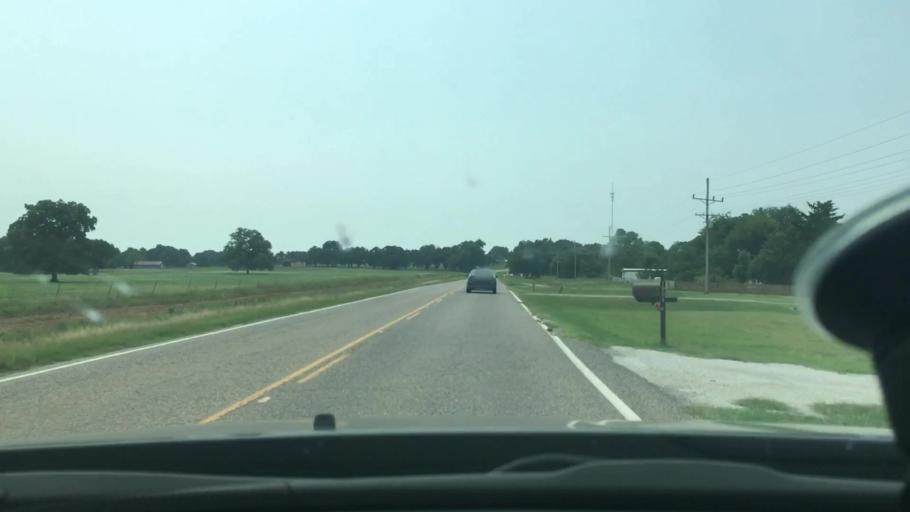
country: US
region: Oklahoma
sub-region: Marshall County
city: Oakland
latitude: 33.9932
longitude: -96.8820
